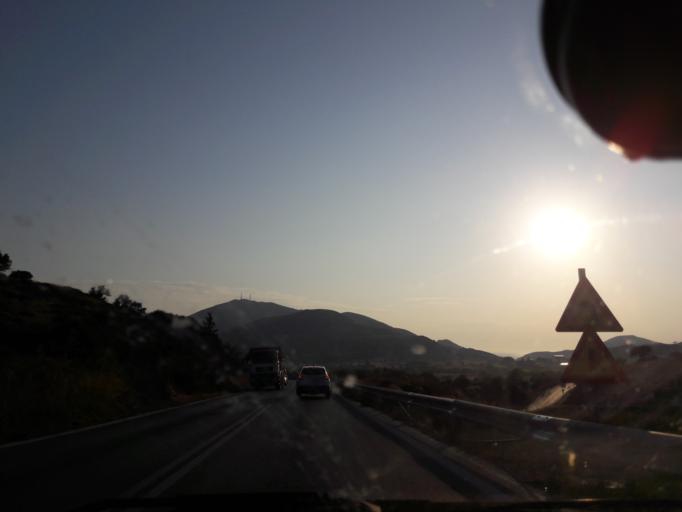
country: GR
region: North Aegean
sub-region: Nomos Lesvou
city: Myrina
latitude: 39.9126
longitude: 25.1151
